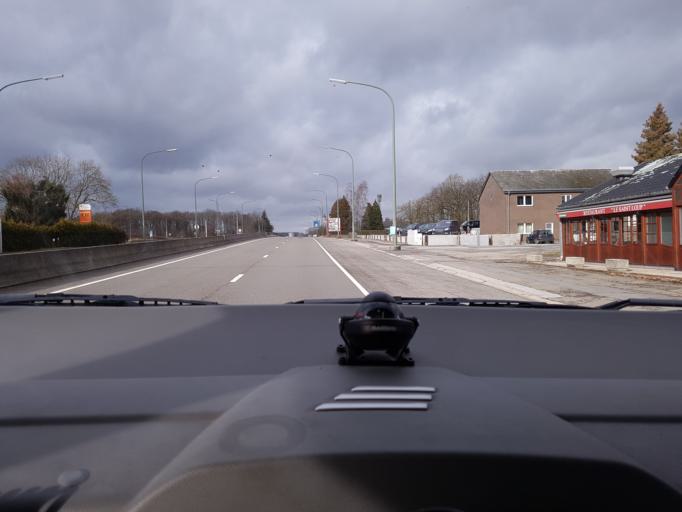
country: BE
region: Wallonia
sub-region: Province du Luxembourg
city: Marche-en-Famenne
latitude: 50.2360
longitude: 5.3006
